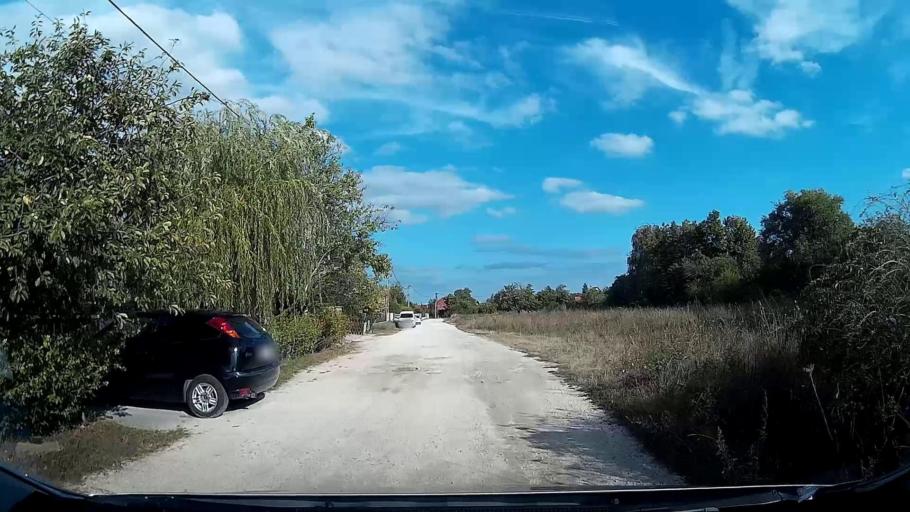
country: HU
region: Pest
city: Nagykovacsi
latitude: 47.6416
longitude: 19.0166
